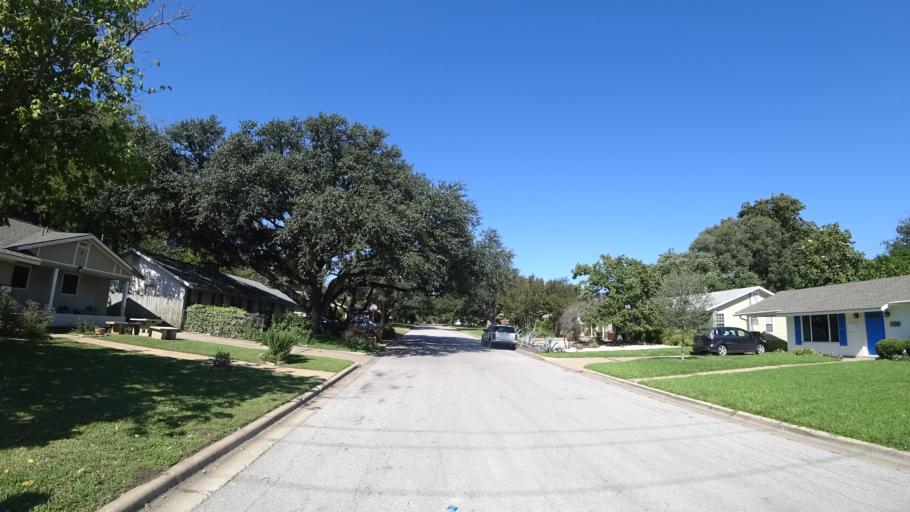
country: US
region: Texas
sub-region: Travis County
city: Austin
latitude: 30.3177
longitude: -97.6905
